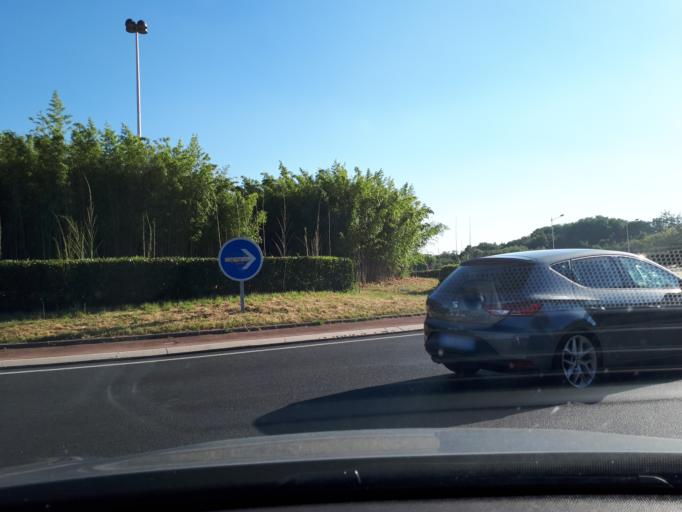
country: FR
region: Rhone-Alpes
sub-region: Departement du Rhone
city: Meyzieu
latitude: 45.7532
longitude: 5.0190
